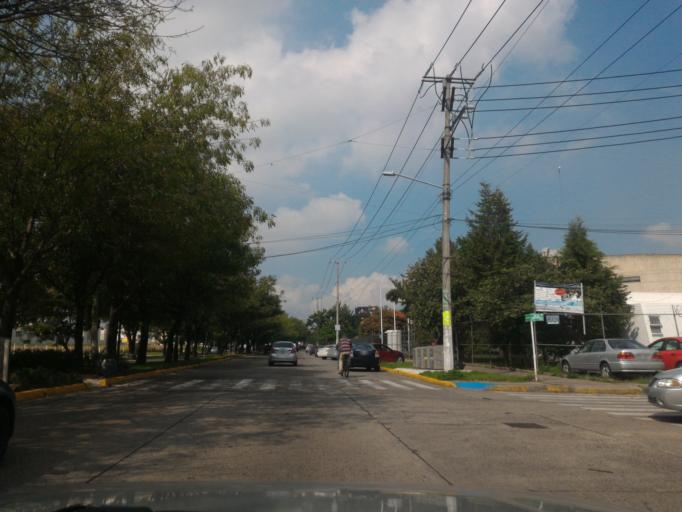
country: MX
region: Jalisco
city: Guadalajara
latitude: 20.6286
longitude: -103.3960
